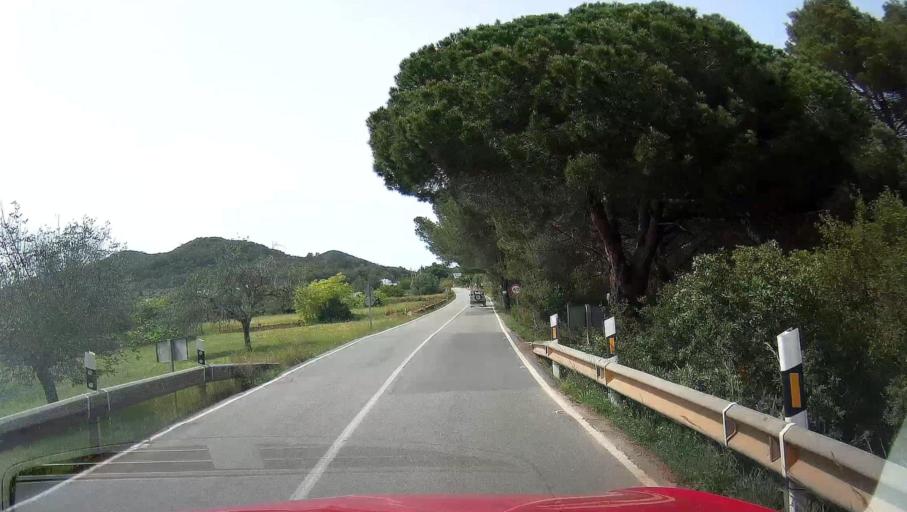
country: ES
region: Balearic Islands
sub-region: Illes Balears
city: Santa Eularia des Riu
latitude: 38.9876
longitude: 1.4895
